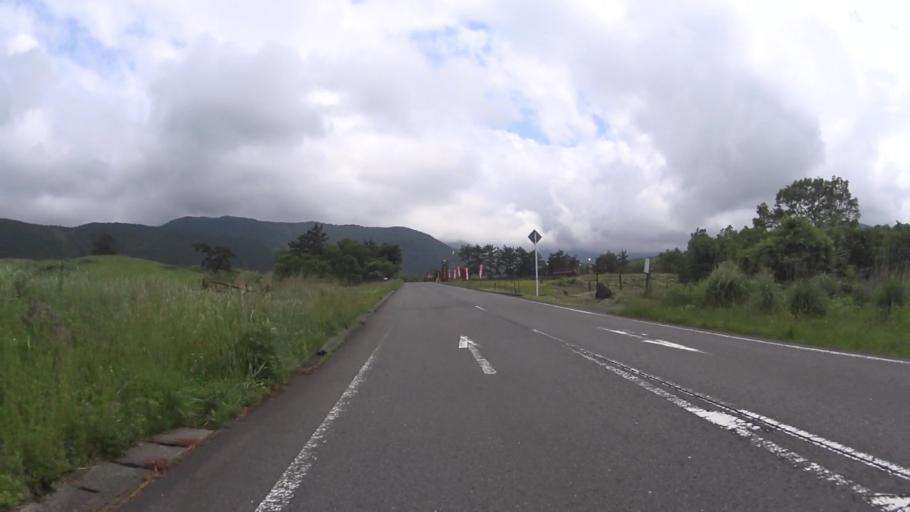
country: JP
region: Oita
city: Tsukawaki
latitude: 33.1439
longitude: 131.2397
